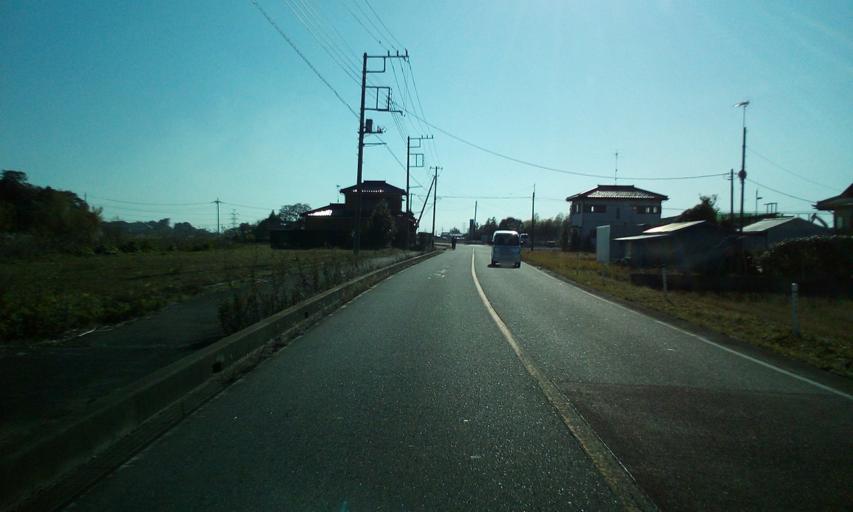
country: JP
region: Ibaraki
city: Sakai
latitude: 36.0667
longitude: 139.7794
